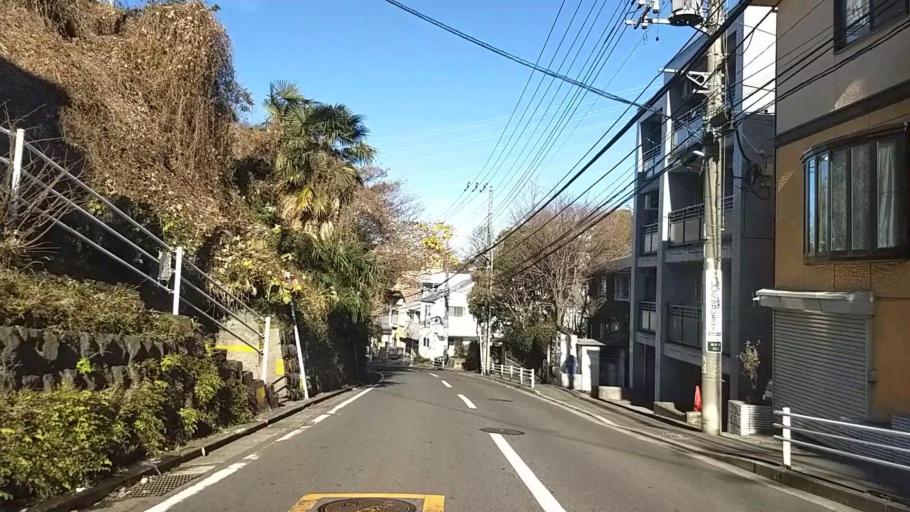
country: JP
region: Kanagawa
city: Yokohama
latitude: 35.4408
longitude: 139.5976
